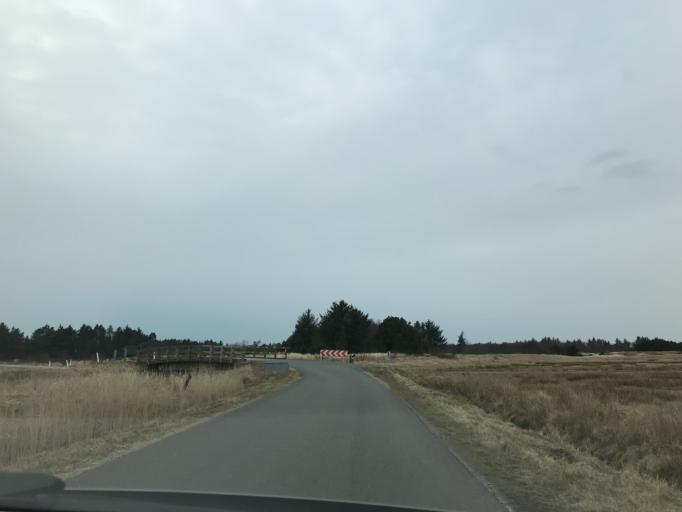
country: DK
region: South Denmark
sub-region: Varde Kommune
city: Oksbol
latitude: 55.8195
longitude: 8.2252
